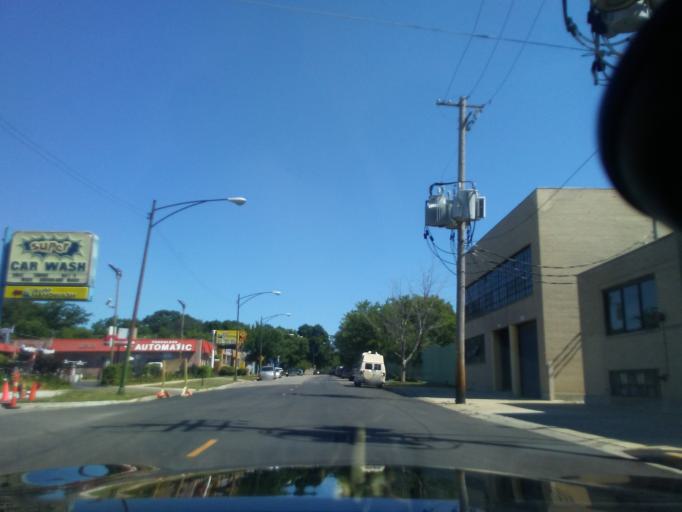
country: US
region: Illinois
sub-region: Cook County
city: Lincolnwood
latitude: 41.9805
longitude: -87.6795
